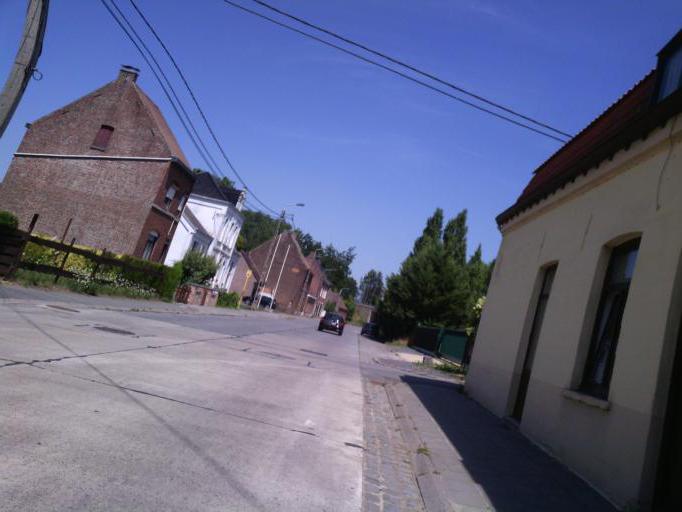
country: BE
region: Wallonia
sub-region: Province du Hainaut
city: Tournai
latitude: 50.6112
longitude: 3.4252
